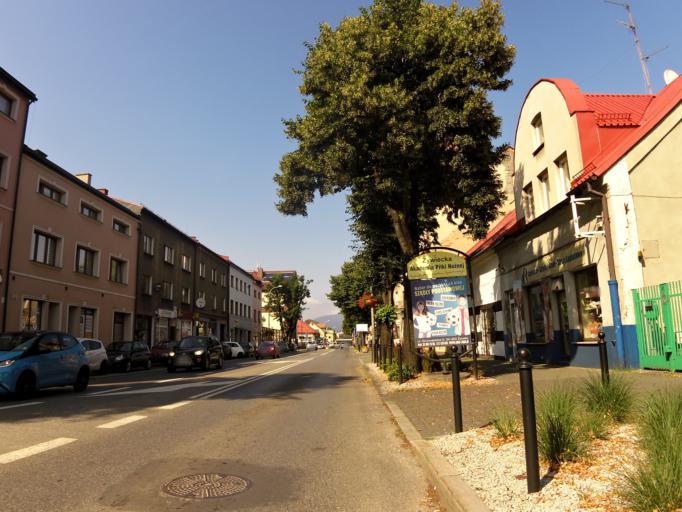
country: PL
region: Silesian Voivodeship
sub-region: Powiat zywiecki
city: Zywiec
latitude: 49.6807
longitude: 19.1881
